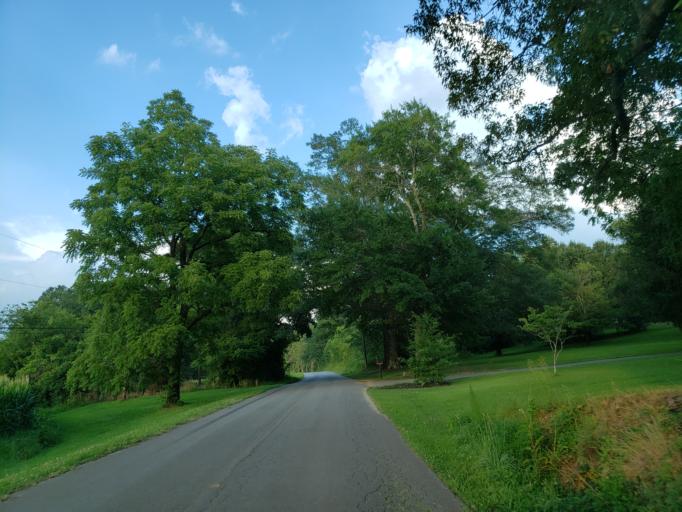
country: US
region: Georgia
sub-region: Polk County
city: Aragon
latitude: 34.0551
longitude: -84.9880
